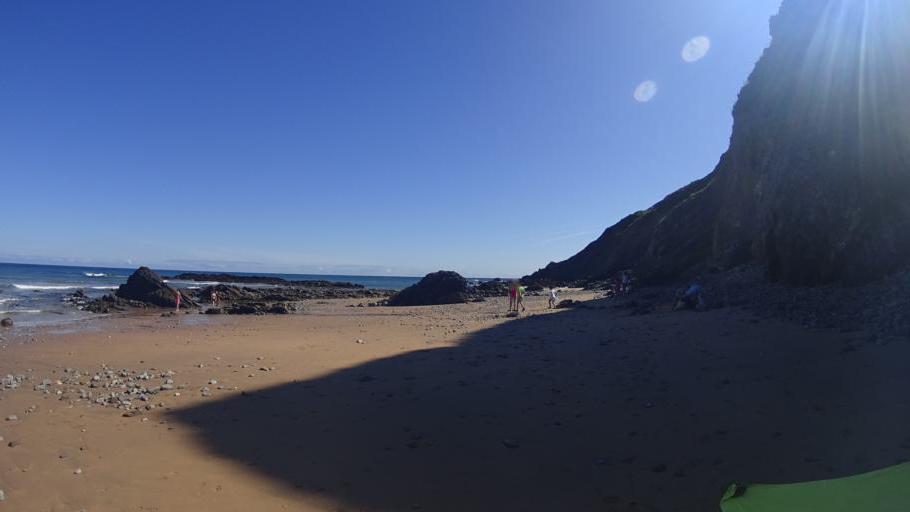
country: ES
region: Asturias
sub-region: Province of Asturias
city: Ribadesella
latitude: 43.4812
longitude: -5.1343
